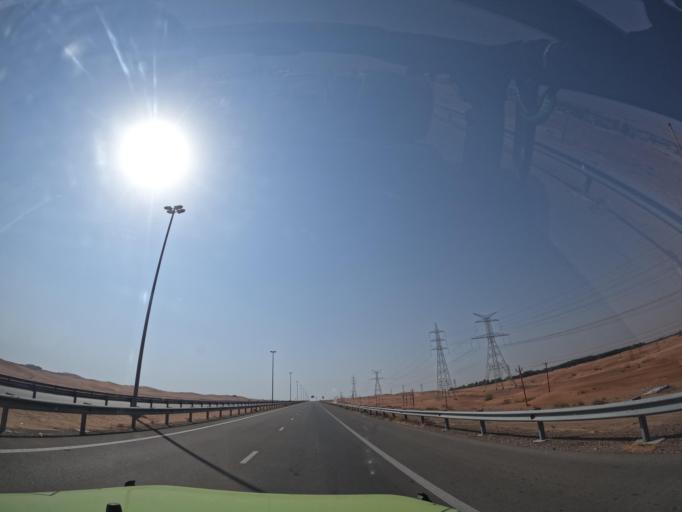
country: OM
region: Al Buraimi
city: Al Buraymi
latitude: 24.3539
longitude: 55.7350
